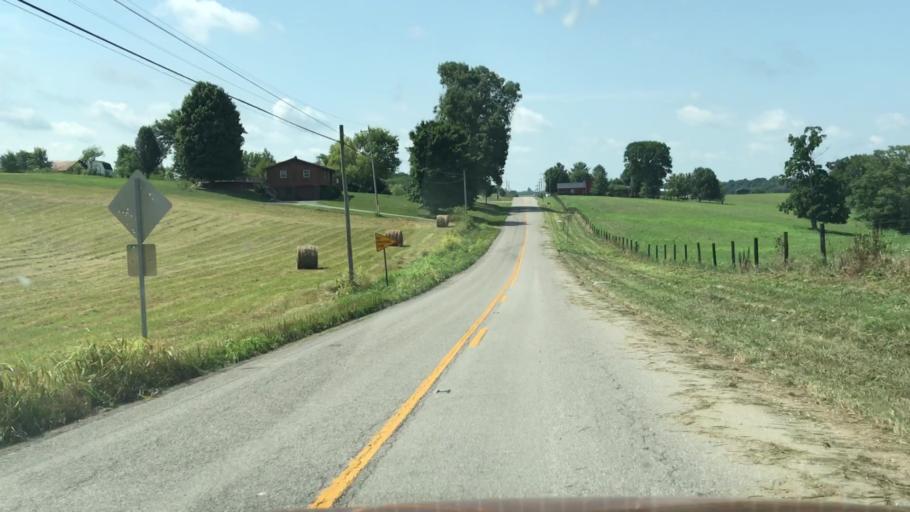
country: US
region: Kentucky
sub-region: Barren County
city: Glasgow
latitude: 36.8781
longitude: -85.8480
